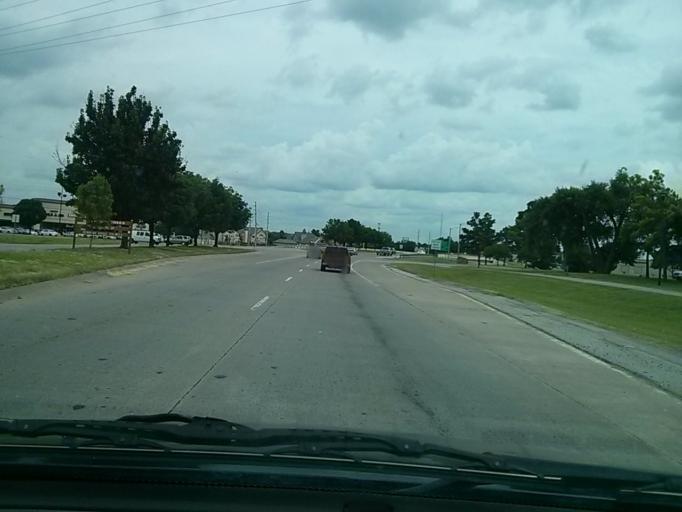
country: US
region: Oklahoma
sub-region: Tulsa County
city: Jenks
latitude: 36.0251
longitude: -95.9503
